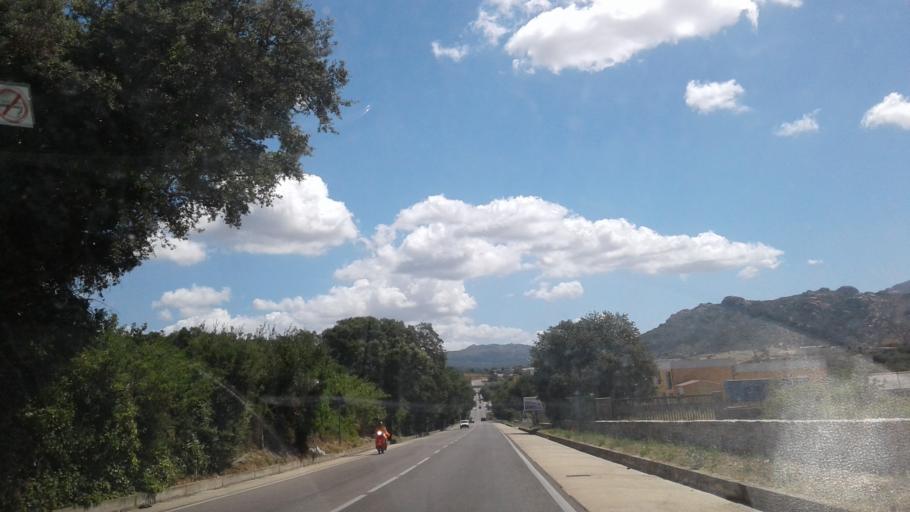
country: IT
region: Sardinia
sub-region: Provincia di Olbia-Tempio
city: Tempio Pausania
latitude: 40.9063
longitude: 9.1357
